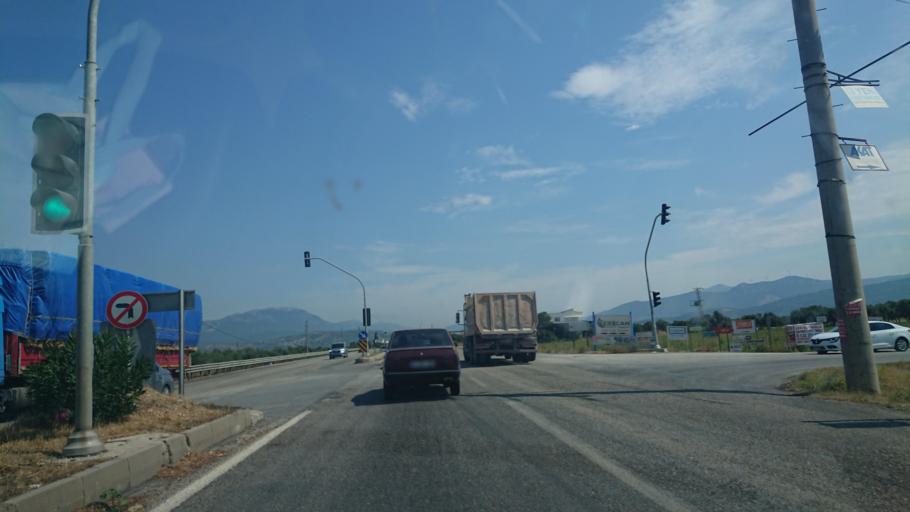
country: TR
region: Izmir
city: Torbali
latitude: 38.2145
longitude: 27.3689
